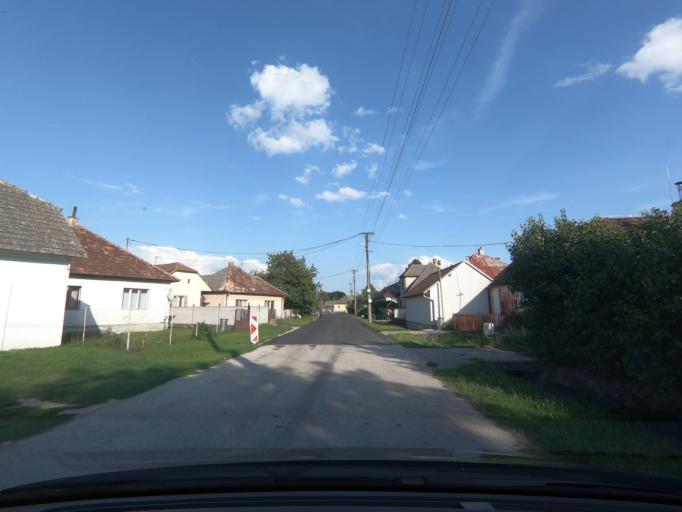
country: SK
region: Nitriansky
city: Stara Tura
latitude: 48.7375
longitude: 17.7054
